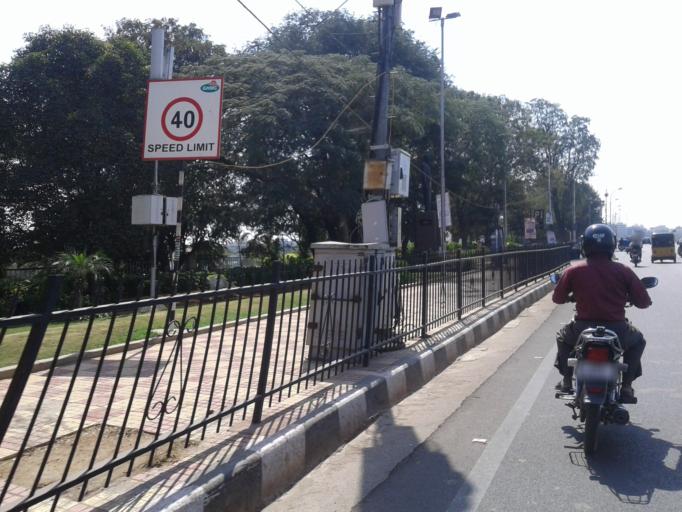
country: IN
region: Telangana
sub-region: Hyderabad
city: Hyderabad
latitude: 17.4169
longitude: 78.4808
